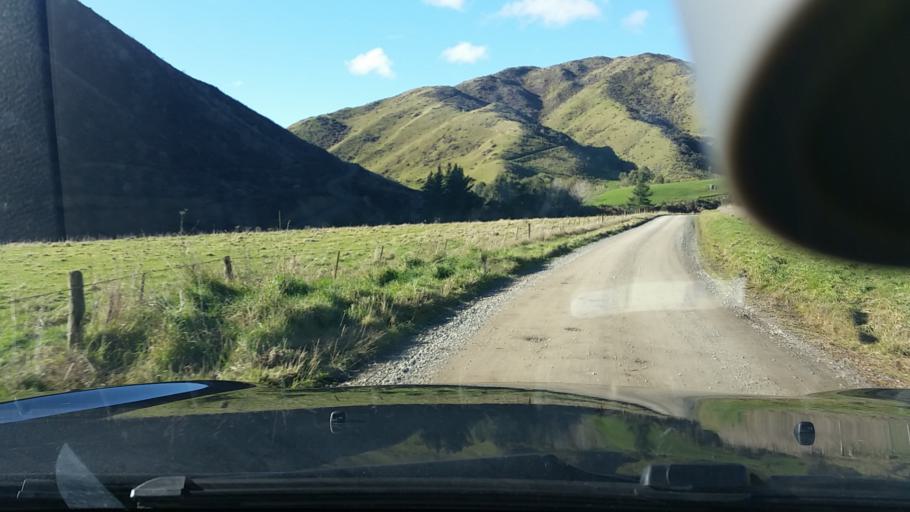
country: NZ
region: Marlborough
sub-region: Marlborough District
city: Blenheim
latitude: -41.6035
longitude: 173.9691
